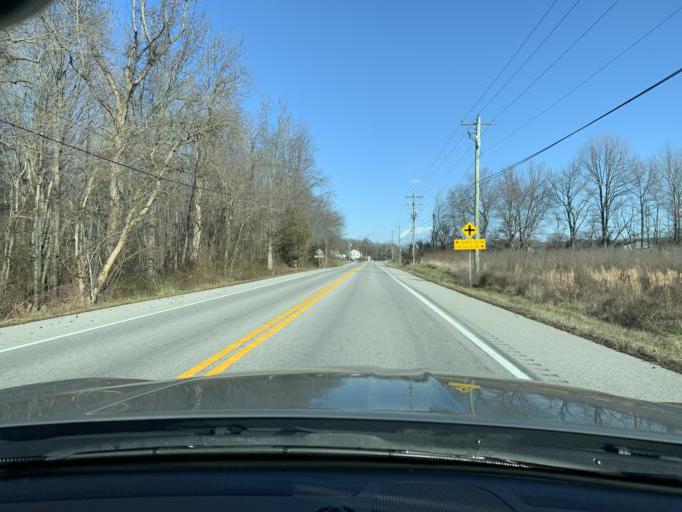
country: US
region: Maryland
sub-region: Queen Anne's County
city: Centreville
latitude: 39.1187
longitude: -76.0170
